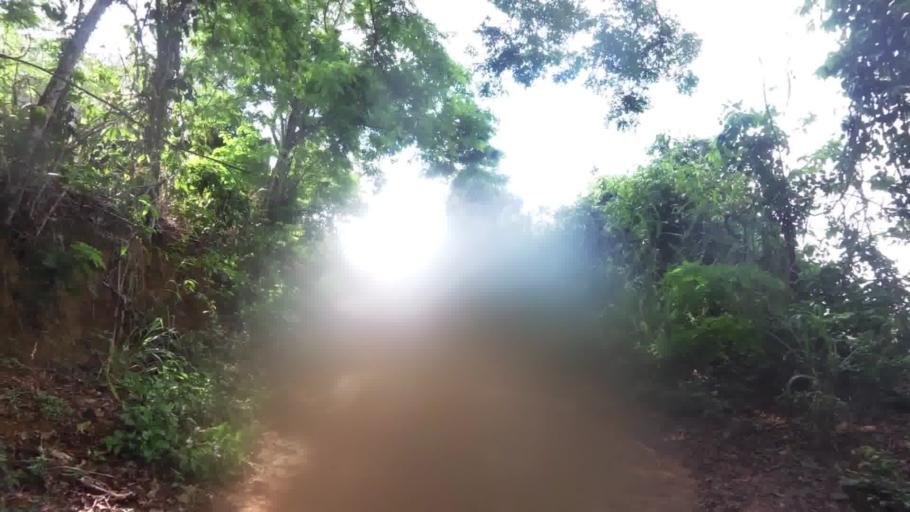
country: BR
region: Espirito Santo
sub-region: Piuma
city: Piuma
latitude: -20.8289
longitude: -40.6952
